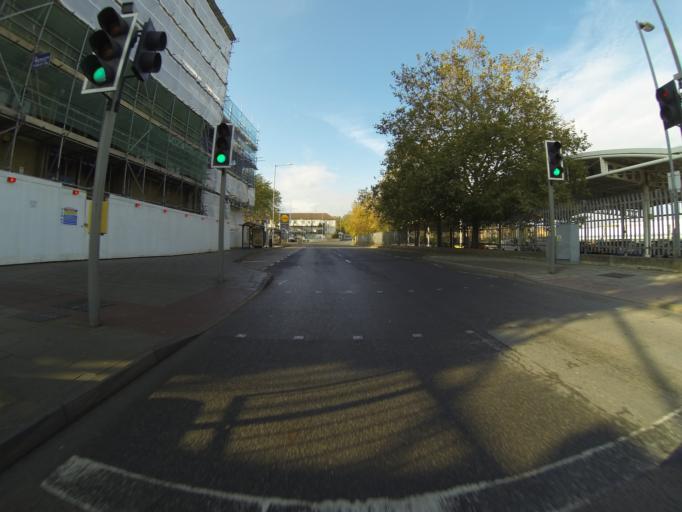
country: GB
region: England
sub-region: Kent
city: Dartford
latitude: 51.4426
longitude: 0.2155
